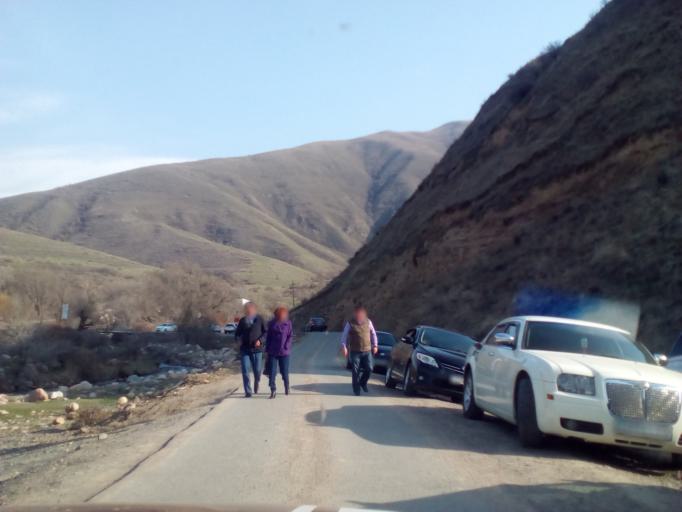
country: KZ
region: Almaty Oblysy
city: Burunday
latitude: 43.1512
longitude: 76.5713
